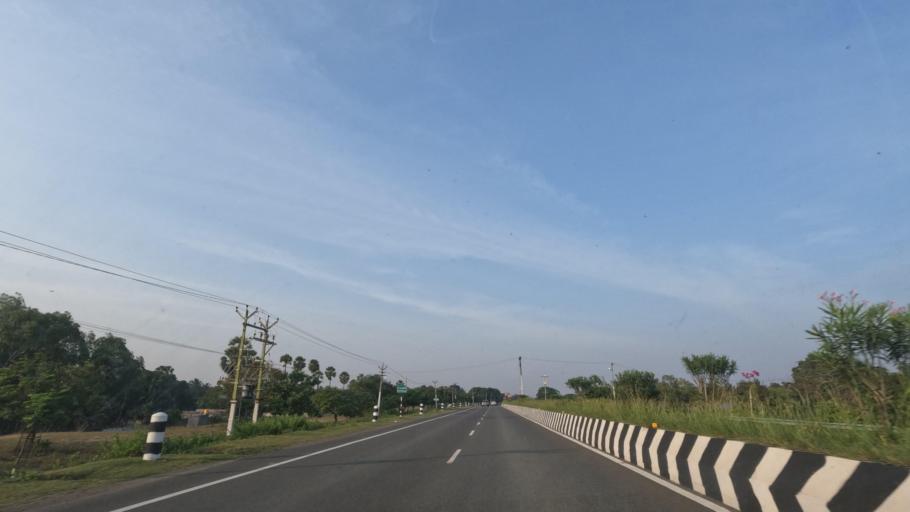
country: IN
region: Tamil Nadu
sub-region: Kancheepuram
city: Mamallapuram
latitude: 12.6822
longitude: 80.2145
